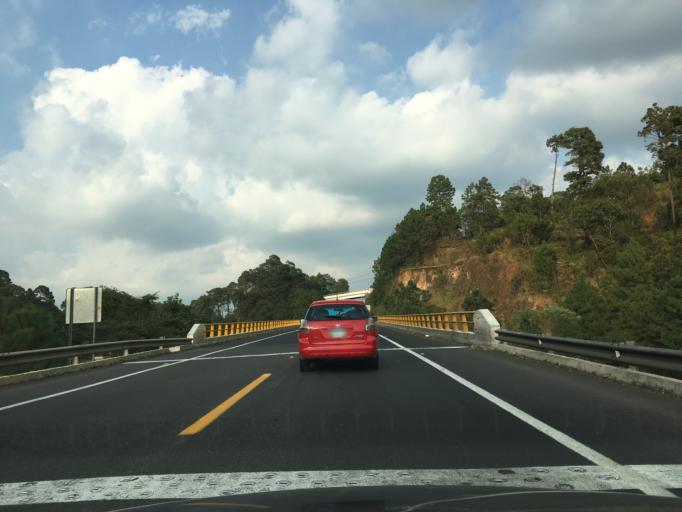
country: MX
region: Michoacan
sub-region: Ziracuaretiro
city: Patuan
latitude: 19.4367
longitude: -101.8890
